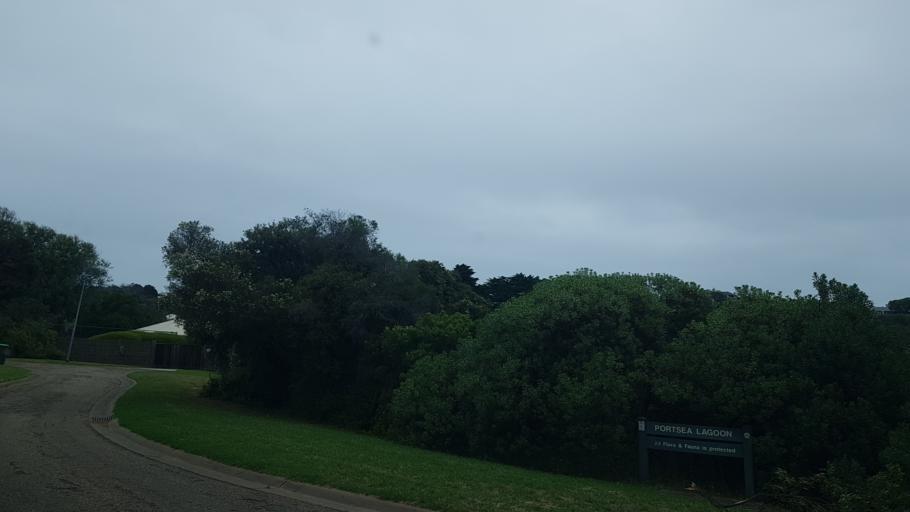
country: AU
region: Victoria
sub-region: Mornington Peninsula
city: Sorrento
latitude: -38.3283
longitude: 144.7150
